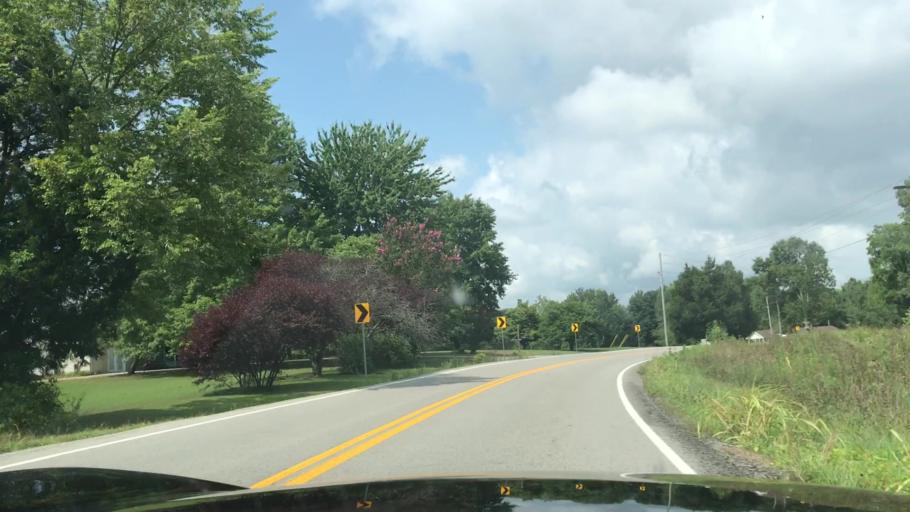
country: US
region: Kentucky
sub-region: Ohio County
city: Beaver Dam
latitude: 37.2043
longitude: -86.9364
